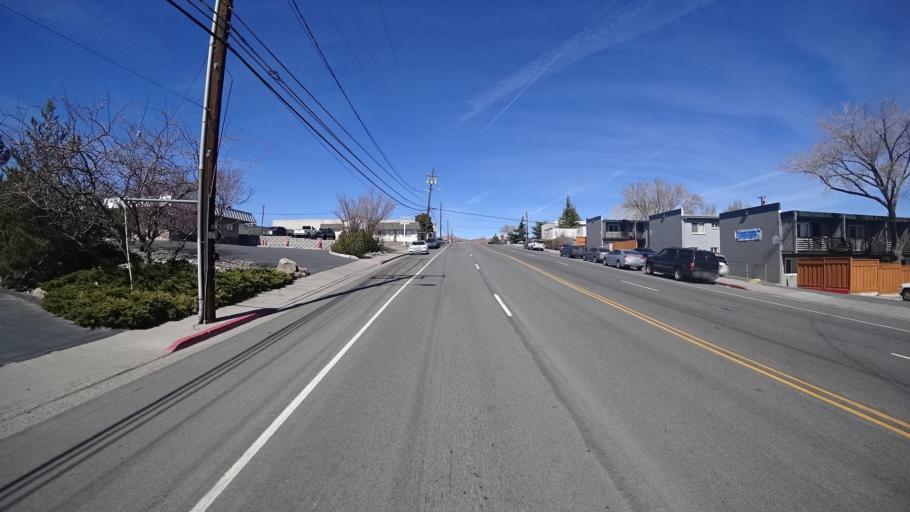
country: US
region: Nevada
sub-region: Washoe County
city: Reno
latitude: 39.5502
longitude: -119.7988
